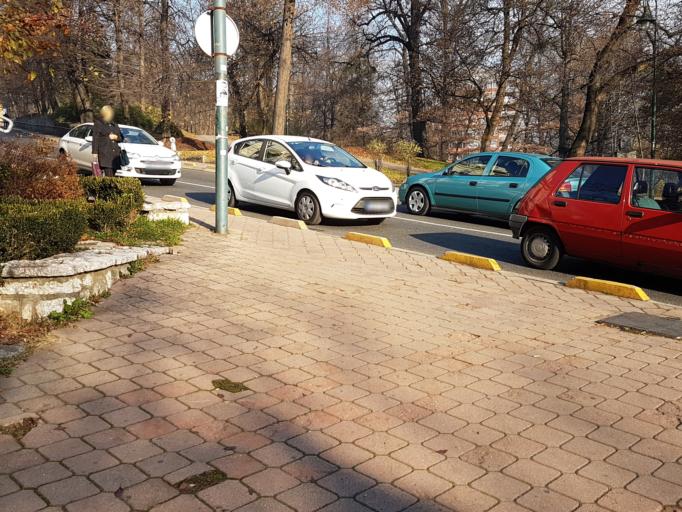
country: BA
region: Federation of Bosnia and Herzegovina
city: Kobilja Glava
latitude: 43.8595
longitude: 18.4147
